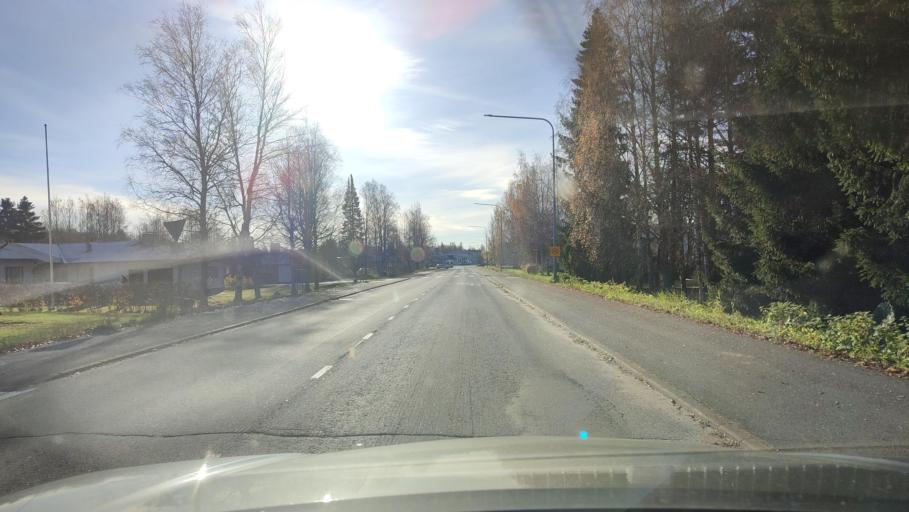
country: FI
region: Southern Ostrobothnia
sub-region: Suupohja
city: Teuva
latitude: 62.4895
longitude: 21.7466
